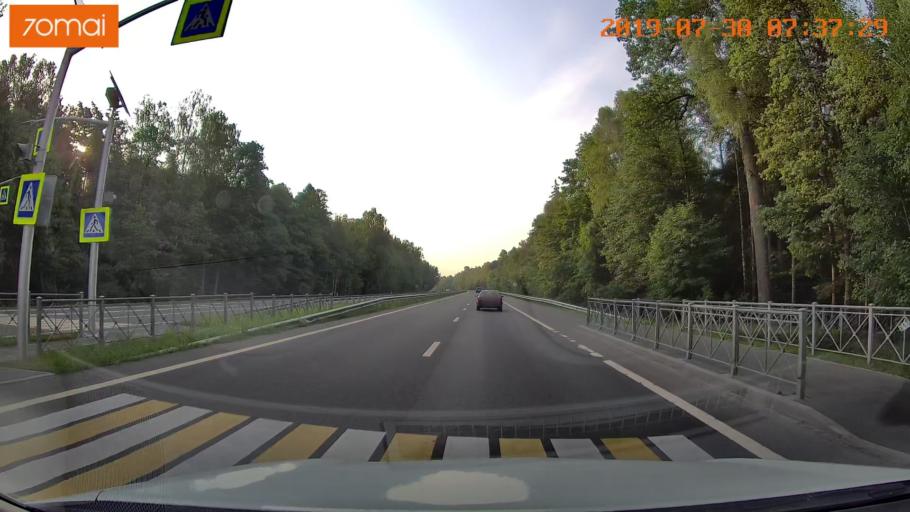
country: RU
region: Kaliningrad
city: Gvardeysk
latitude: 54.6555
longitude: 21.1469
